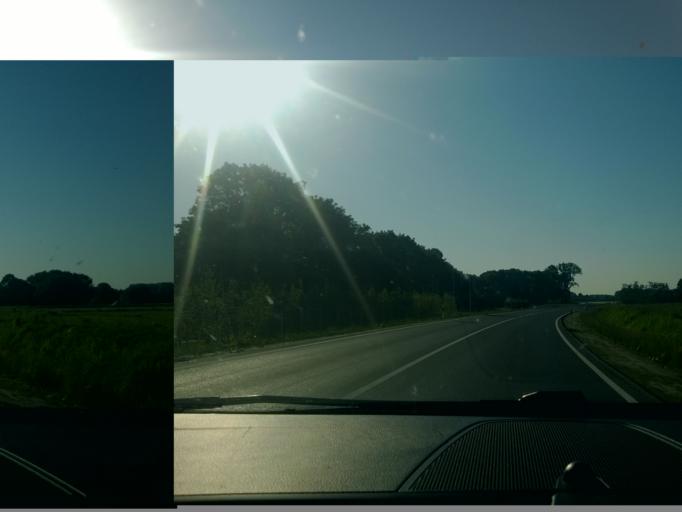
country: DE
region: North Rhine-Westphalia
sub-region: Regierungsbezirk Munster
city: Nottuln
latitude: 51.9380
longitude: 7.3610
